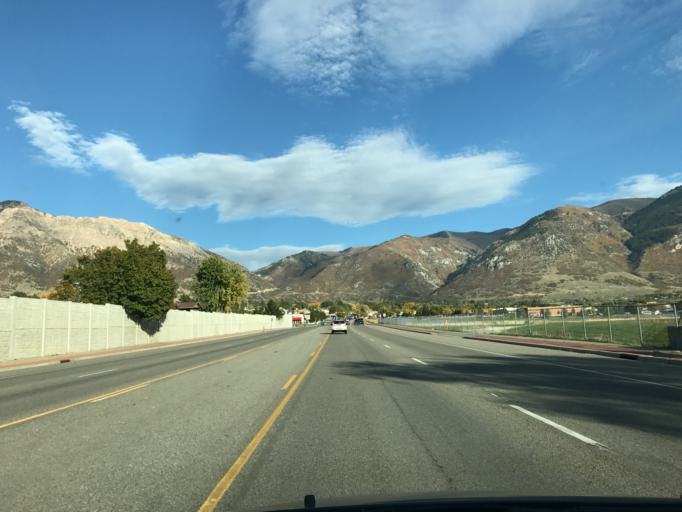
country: US
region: Utah
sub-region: Weber County
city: North Ogden
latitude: 41.3058
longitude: -111.9751
